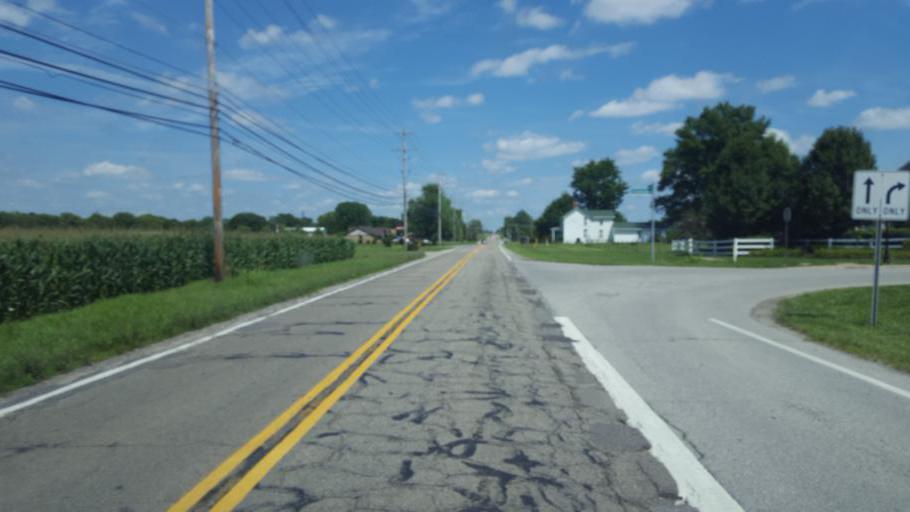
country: US
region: Ohio
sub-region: Franklin County
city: Obetz
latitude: 39.8624
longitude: -82.9963
